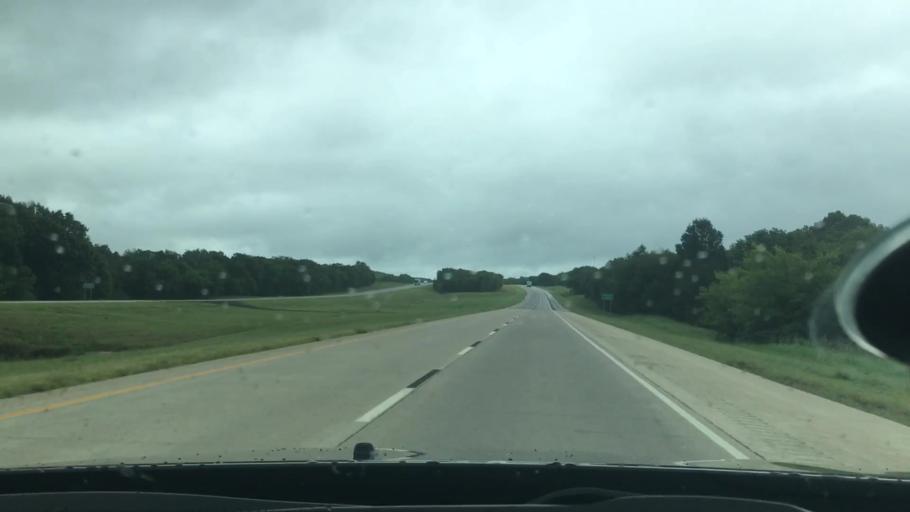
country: US
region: Oklahoma
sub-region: Okmulgee County
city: Henryetta
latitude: 35.4319
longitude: -95.8773
